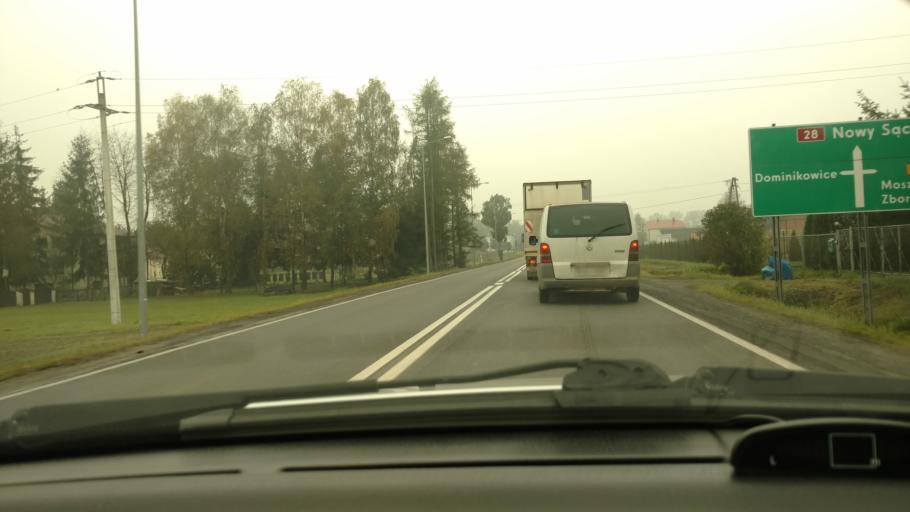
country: PL
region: Lesser Poland Voivodeship
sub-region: Powiat gorlicki
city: Kobylanka
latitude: 49.6913
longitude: 21.1996
